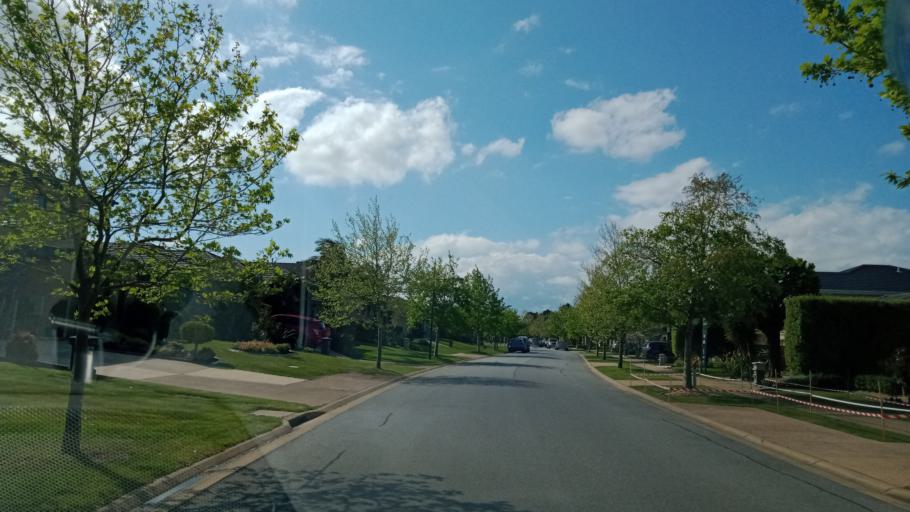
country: AU
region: Victoria
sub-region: Frankston
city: Sandhurst
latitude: -38.0866
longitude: 145.2160
